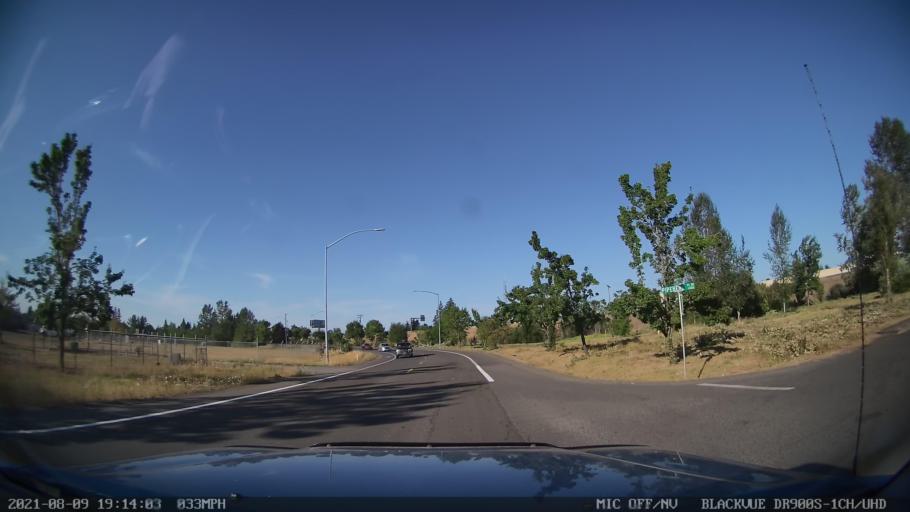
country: US
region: Oregon
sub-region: Marion County
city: Four Corners
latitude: 44.9296
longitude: -122.9928
